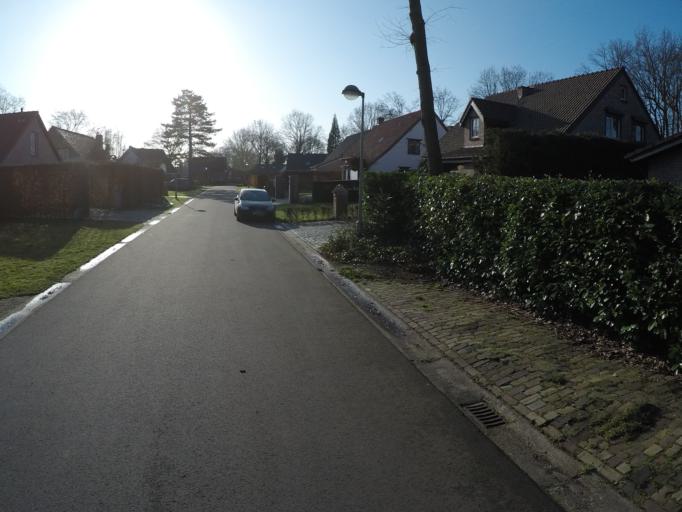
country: BE
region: Flanders
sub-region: Provincie Antwerpen
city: Schilde
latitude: 51.2187
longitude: 4.5889
